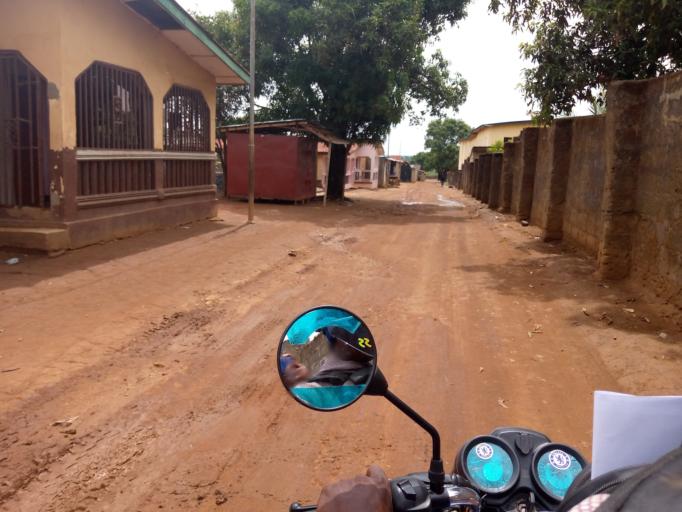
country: SL
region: Western Area
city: Hastings
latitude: 8.4125
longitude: -13.1432
